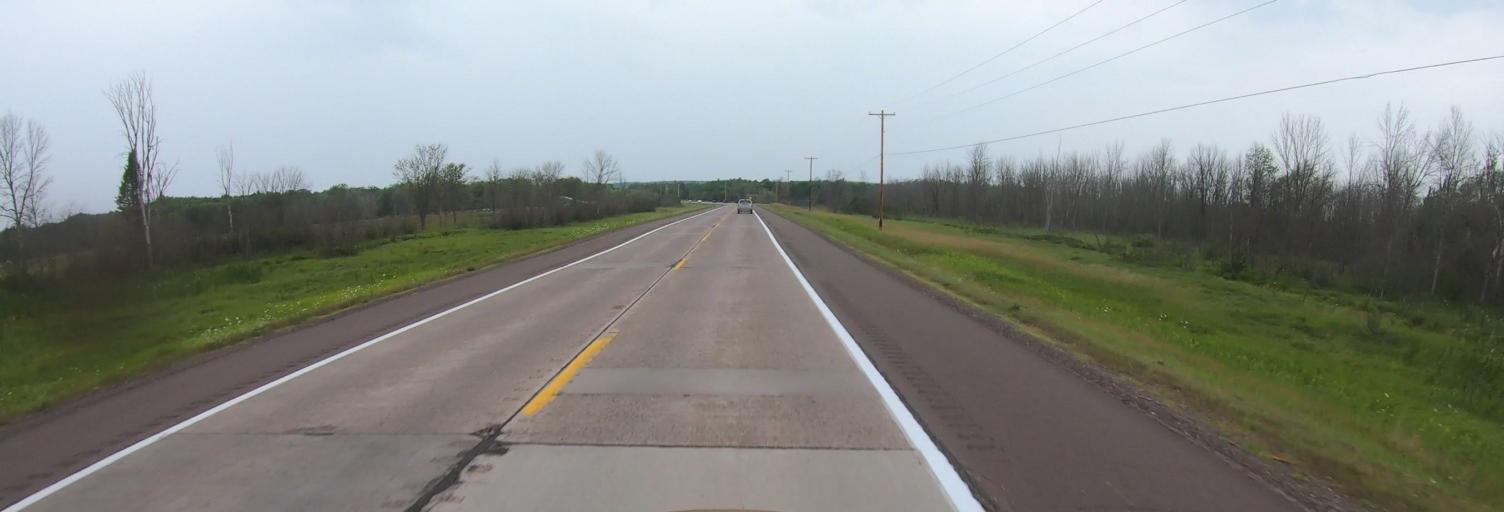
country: US
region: Michigan
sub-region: Houghton County
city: Dollar Bay
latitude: 47.0142
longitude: -88.4997
